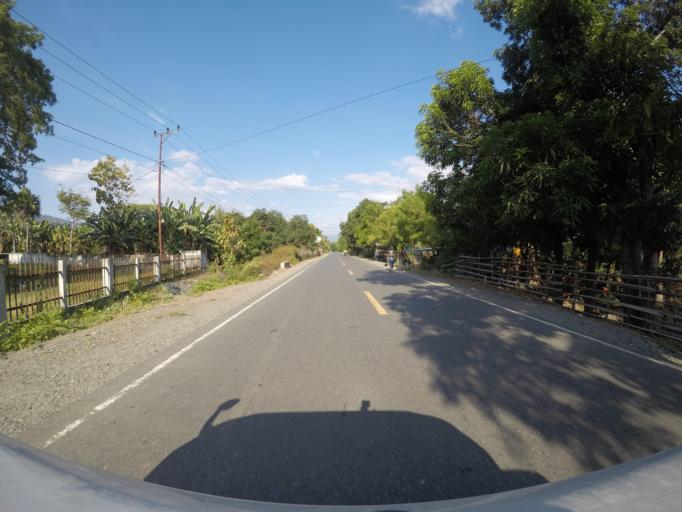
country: TL
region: Liquica
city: Maubara
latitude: -8.7308
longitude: 125.1318
